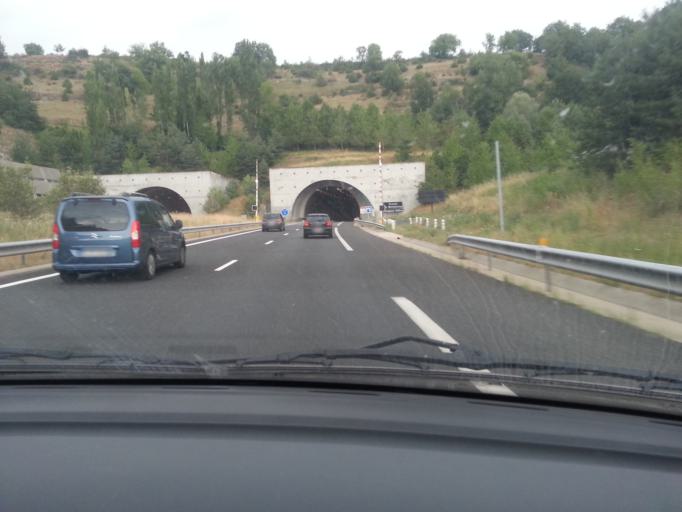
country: FR
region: Languedoc-Roussillon
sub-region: Departement de la Lozere
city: La Canourgue
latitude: 44.4808
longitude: 3.1986
